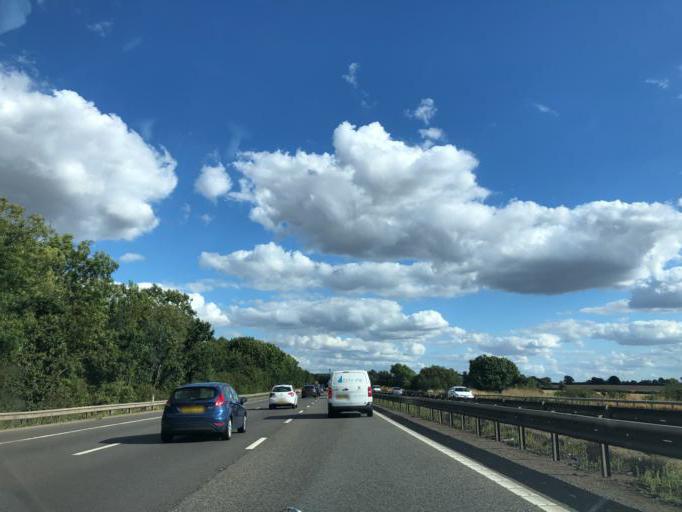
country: GB
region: England
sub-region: Northamptonshire
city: Hartwell
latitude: 52.1422
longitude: -0.8360
